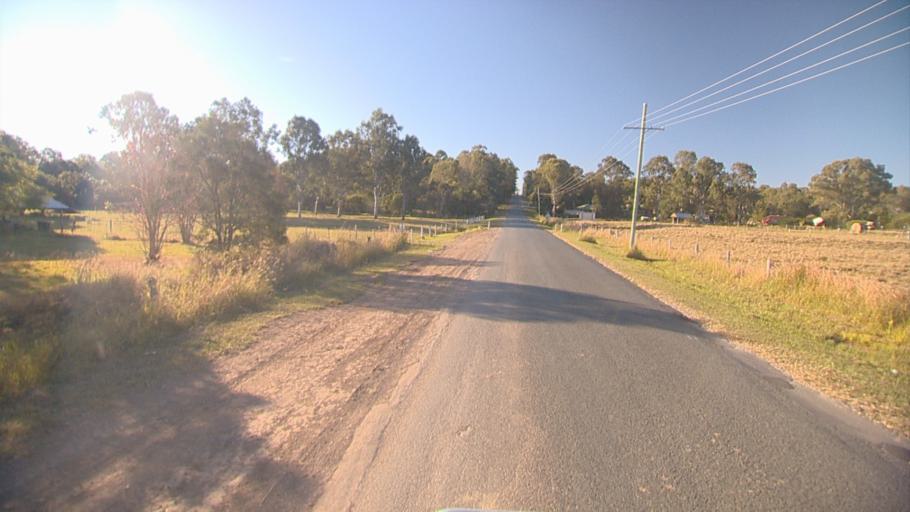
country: AU
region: Queensland
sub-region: Logan
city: Chambers Flat
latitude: -27.7824
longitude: 153.1352
